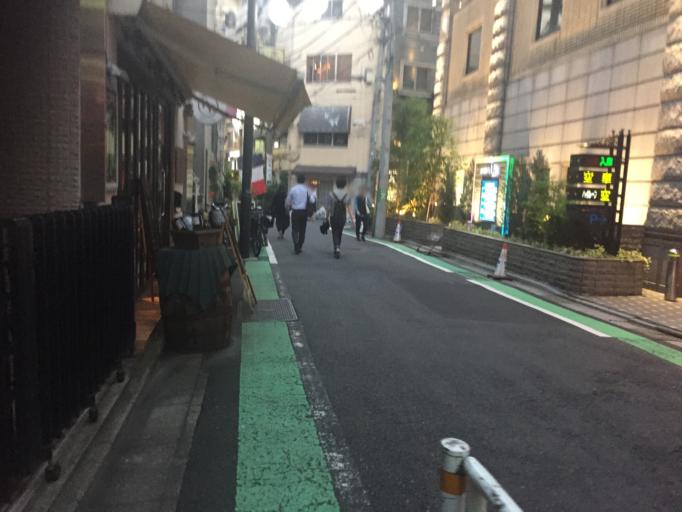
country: JP
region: Tokyo
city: Tokyo
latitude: 35.6460
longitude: 139.7084
